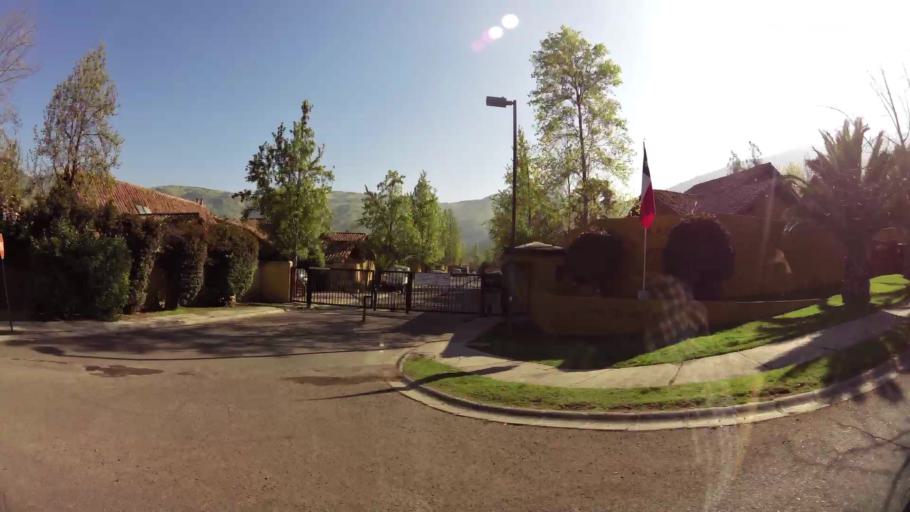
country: CL
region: Santiago Metropolitan
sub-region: Provincia de Chacabuco
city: Chicureo Abajo
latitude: -33.3453
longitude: -70.6649
